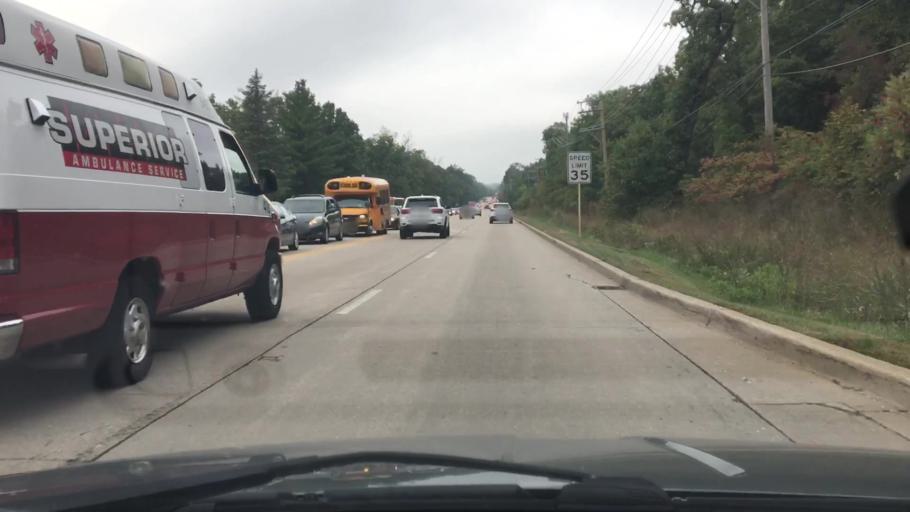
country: US
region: Illinois
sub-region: Lake County
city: Lincolnshire
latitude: 42.2005
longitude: -87.9066
